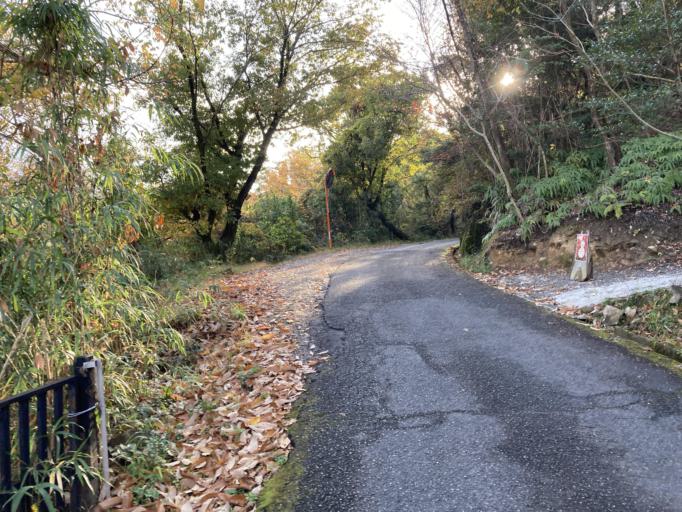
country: JP
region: Nara
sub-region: Ikoma-shi
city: Ikoma
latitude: 34.6780
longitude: 135.6917
